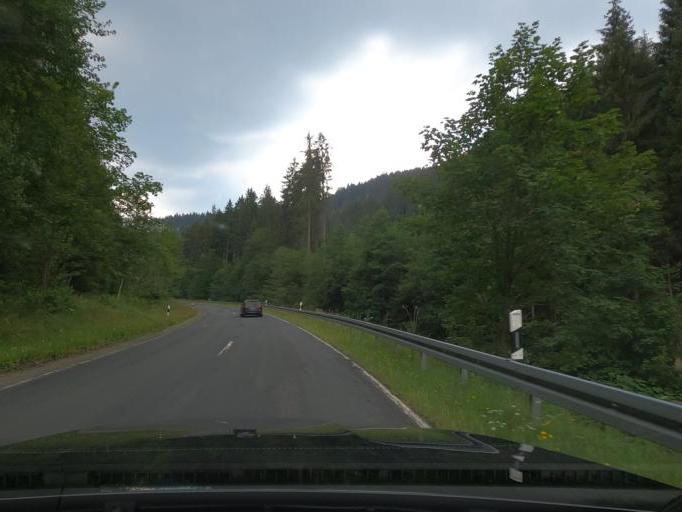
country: DE
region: Lower Saxony
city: Wildemann
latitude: 51.8390
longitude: 10.2631
